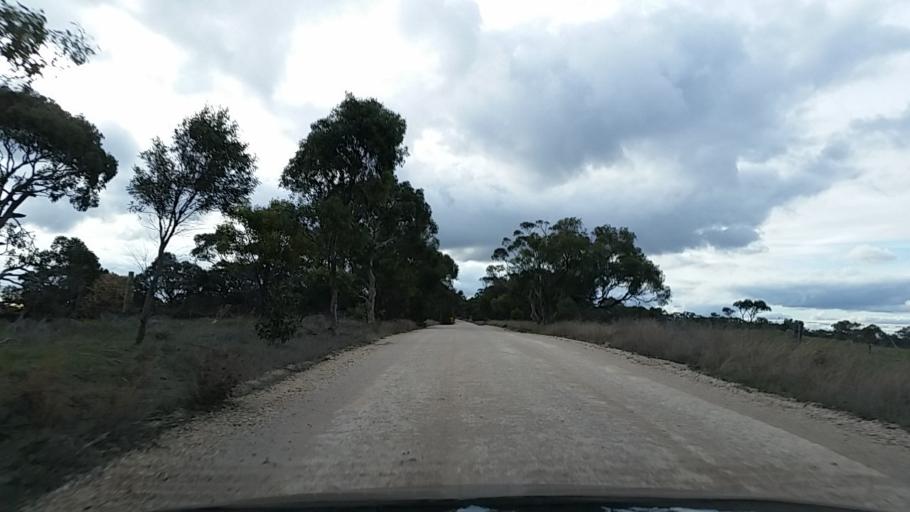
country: AU
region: South Australia
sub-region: Mount Barker
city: Callington
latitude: -35.0017
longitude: 139.0604
